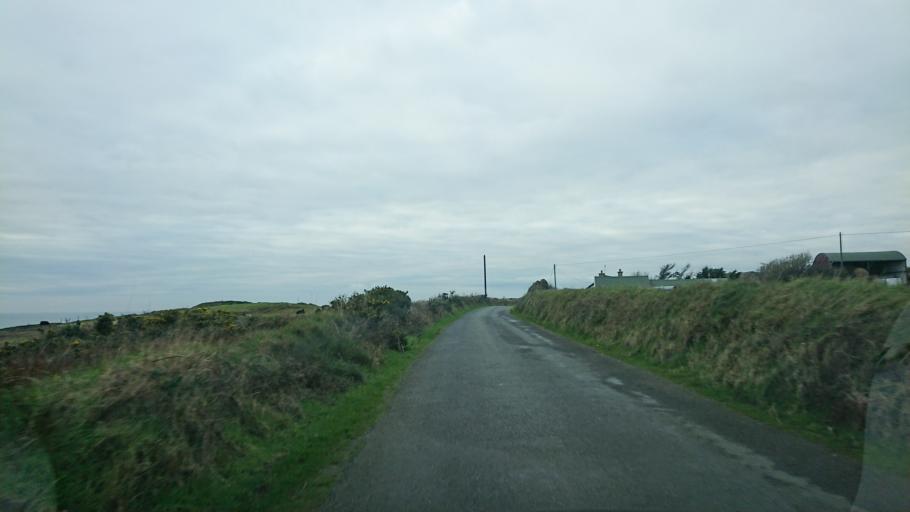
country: IE
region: Munster
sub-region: Waterford
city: Tra Mhor
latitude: 52.1390
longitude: -7.1767
